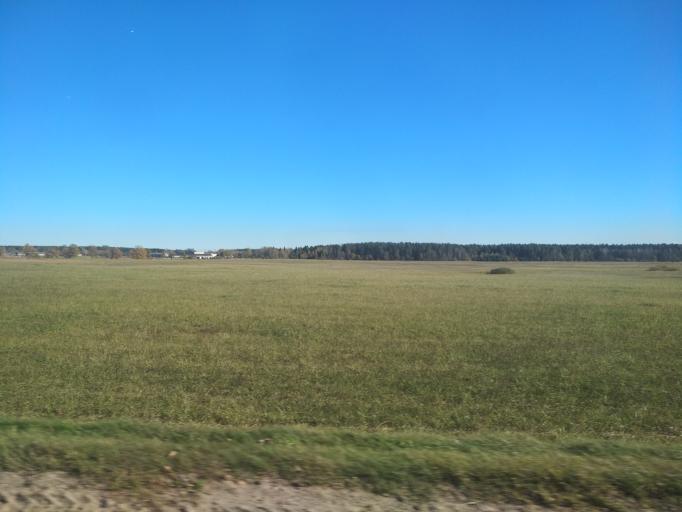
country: BY
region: Minsk
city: Il'ya
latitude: 54.5596
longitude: 27.2129
